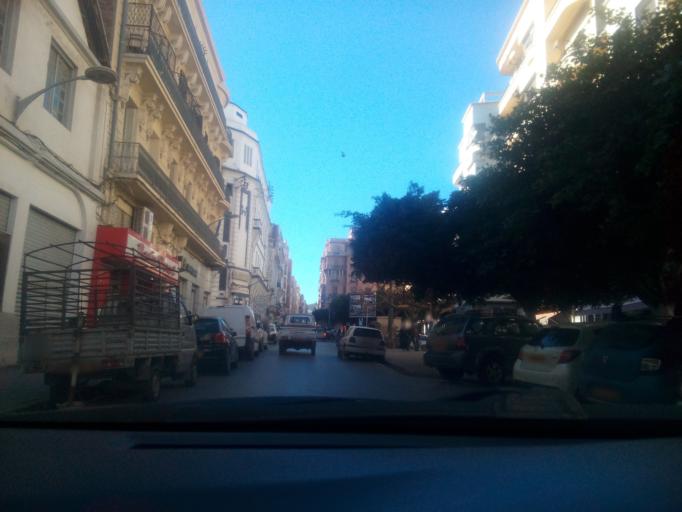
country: DZ
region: Oran
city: Oran
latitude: 35.7040
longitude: -0.6402
